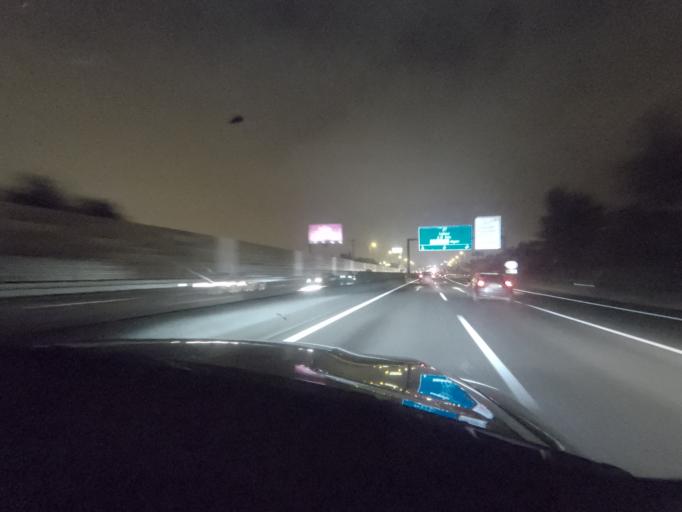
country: PT
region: Lisbon
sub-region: Loures
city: Santa Iria da Azoia
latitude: 38.8544
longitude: -9.0848
